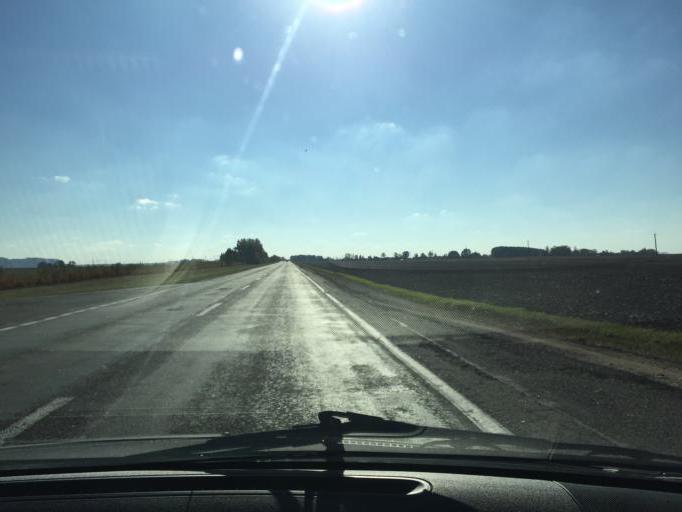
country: BY
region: Minsk
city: Slutsk
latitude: 52.9251
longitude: 27.4848
